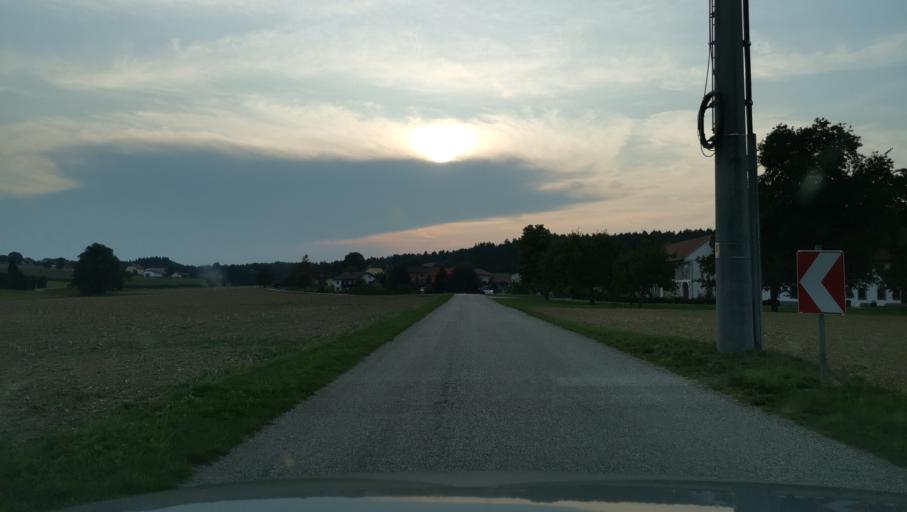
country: AT
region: Upper Austria
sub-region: Politischer Bezirk Grieskirchen
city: Grieskirchen
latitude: 48.3009
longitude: 13.8130
